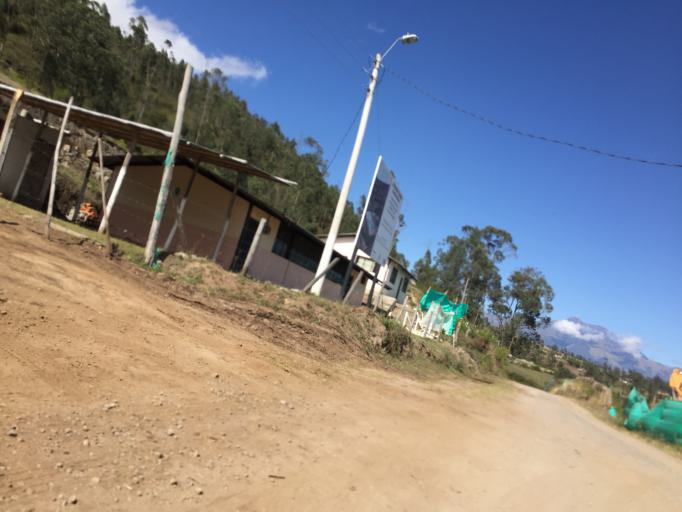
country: EC
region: Imbabura
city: Ibarra
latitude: 0.3098
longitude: -78.1529
